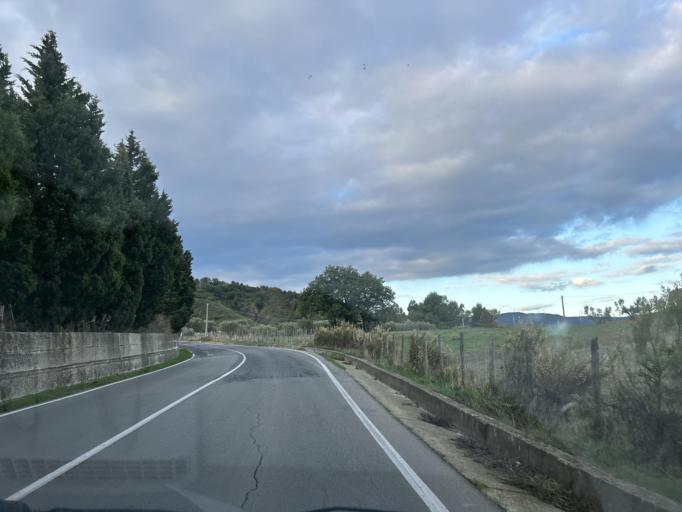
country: IT
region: Calabria
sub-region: Provincia di Catanzaro
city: Montauro
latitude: 38.7593
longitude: 16.5093
